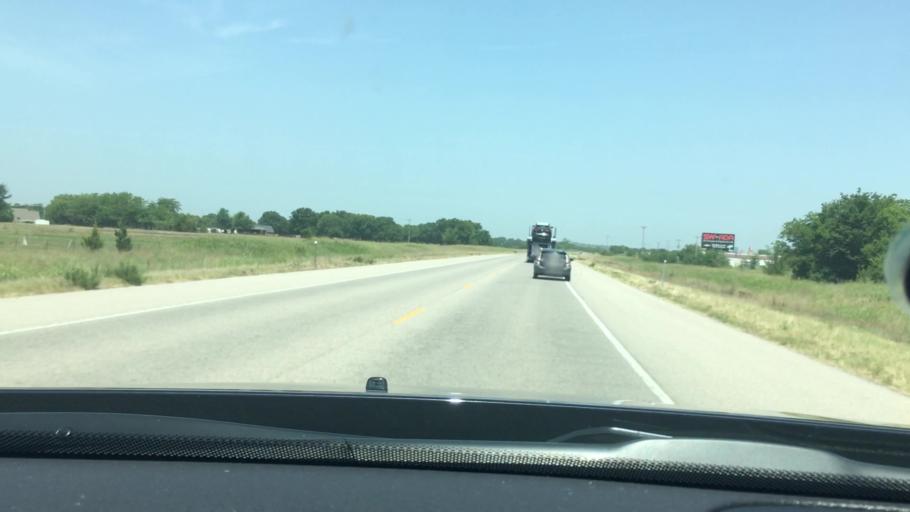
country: US
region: Oklahoma
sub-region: Pontotoc County
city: Ada
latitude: 34.7069
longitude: -96.6115
